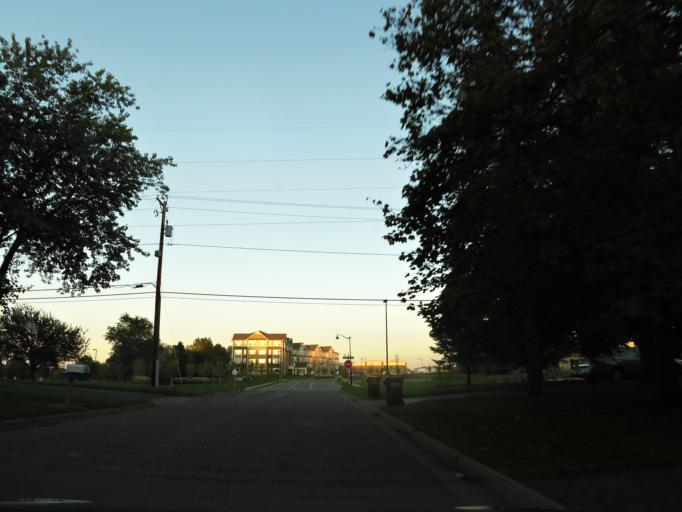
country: US
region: Minnesota
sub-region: Washington County
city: Oakdale
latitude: 44.9649
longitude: -92.9653
